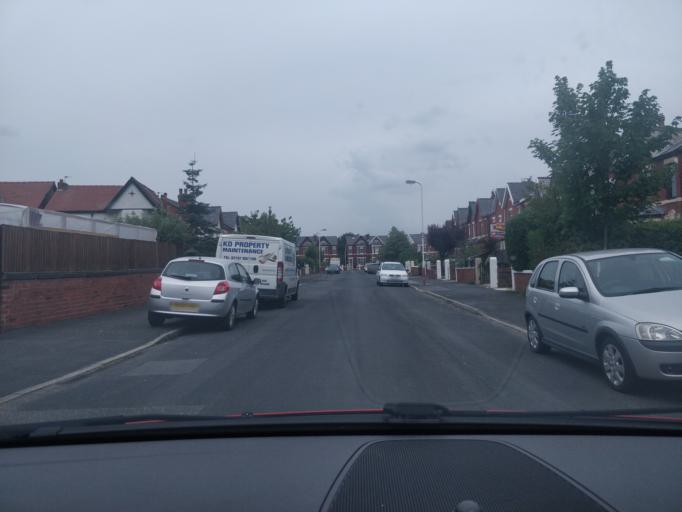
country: GB
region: England
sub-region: Sefton
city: Southport
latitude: 53.6516
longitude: -2.9690
